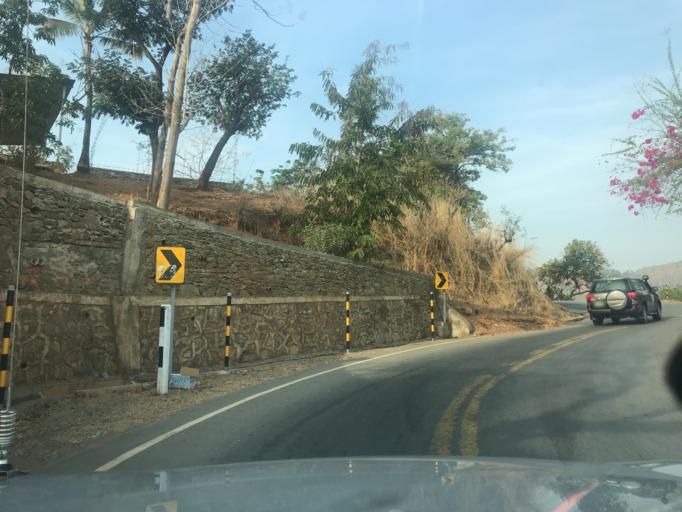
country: TL
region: Dili
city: Dili
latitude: -8.5721
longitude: 125.5882
